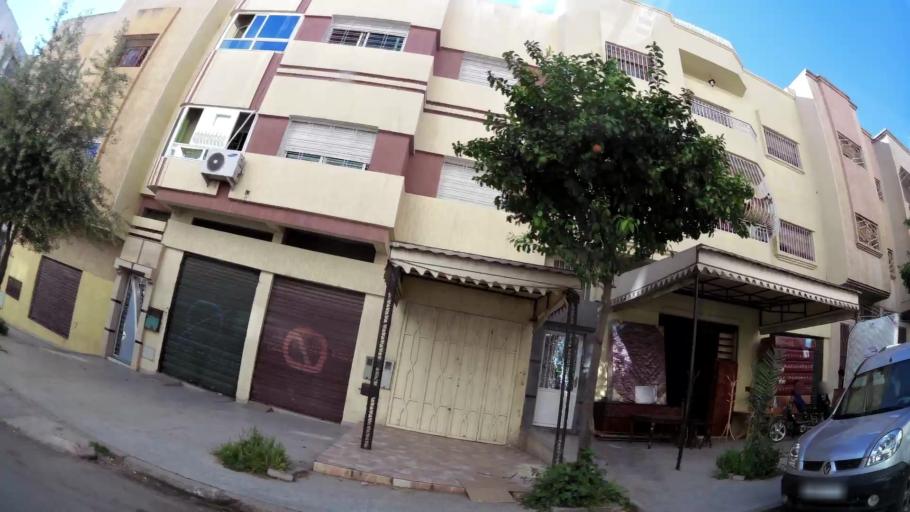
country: MA
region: Fes-Boulemane
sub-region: Fes
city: Fes
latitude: 34.0129
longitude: -4.9676
